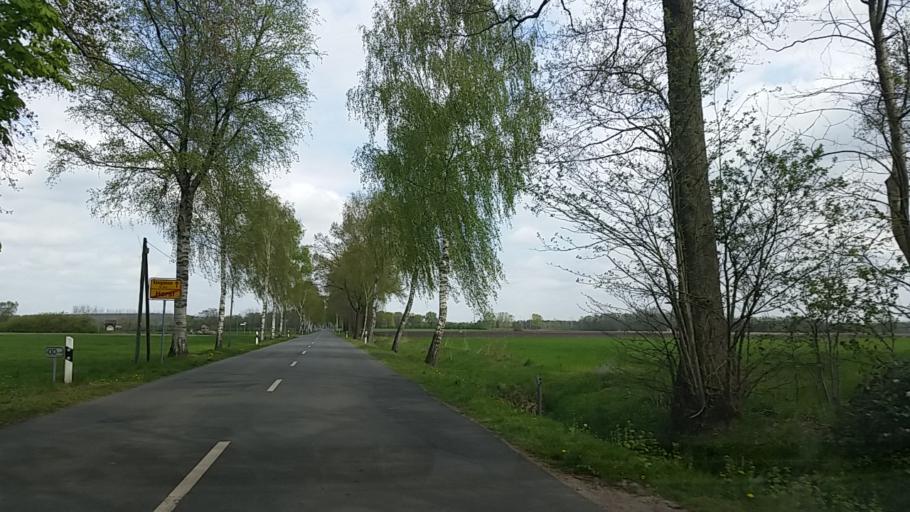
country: DE
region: Lower Saxony
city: Konigsmoor
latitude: 53.2056
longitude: 9.7084
